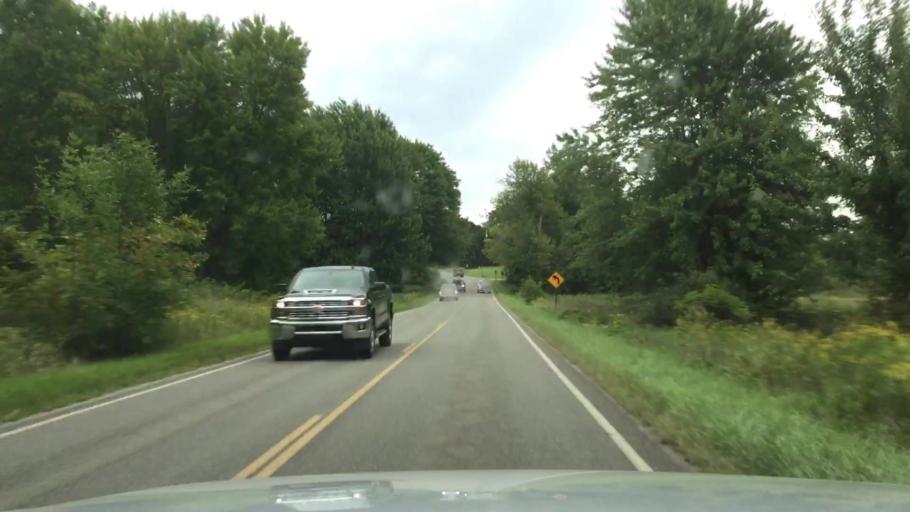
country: US
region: Michigan
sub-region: Genesee County
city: Argentine
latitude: 42.8173
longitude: -83.9350
